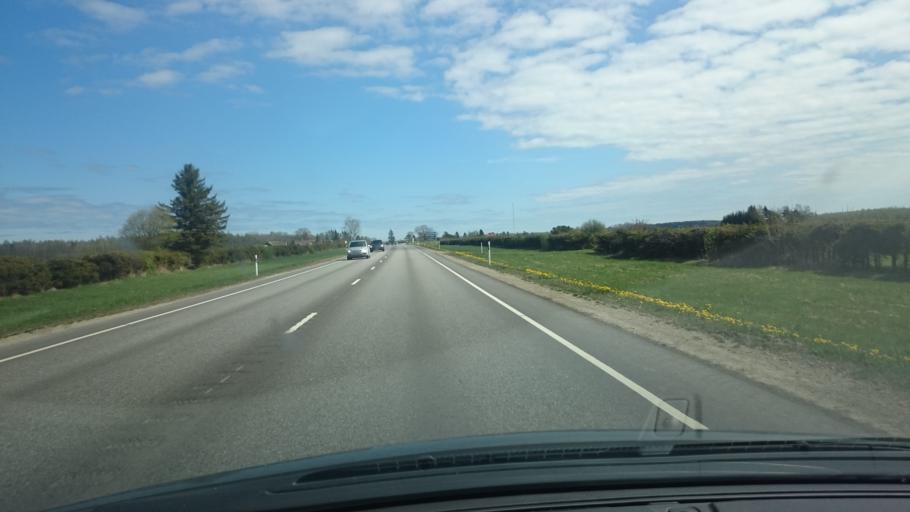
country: EE
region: Ida-Virumaa
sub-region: Kohtla-Nomme vald
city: Kohtla-Nomme
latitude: 59.4191
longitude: 27.1648
